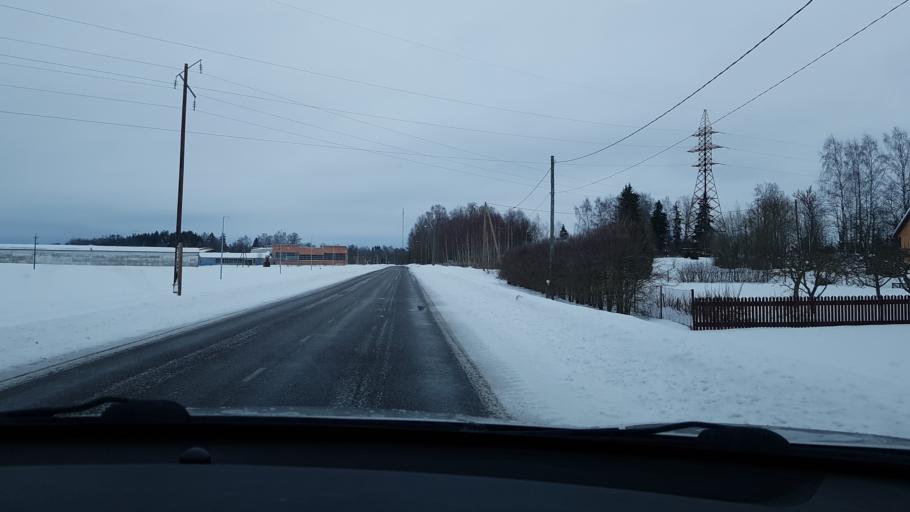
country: EE
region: Jaervamaa
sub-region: Jaerva-Jaani vald
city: Jarva-Jaani
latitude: 59.1347
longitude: 25.7478
